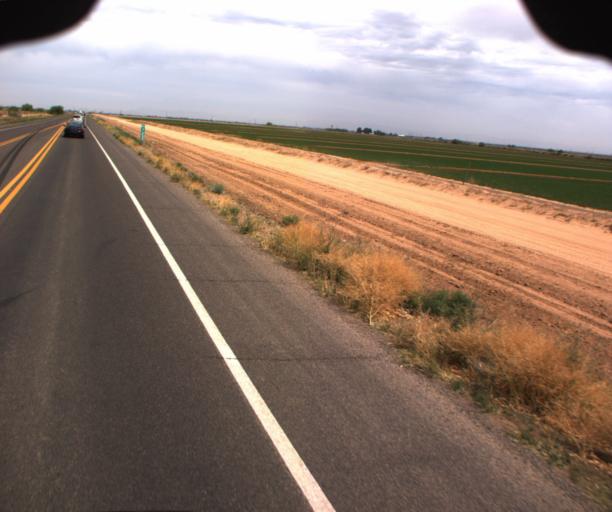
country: US
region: Arizona
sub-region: Pinal County
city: Eloy
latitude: 32.8222
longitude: -111.5153
